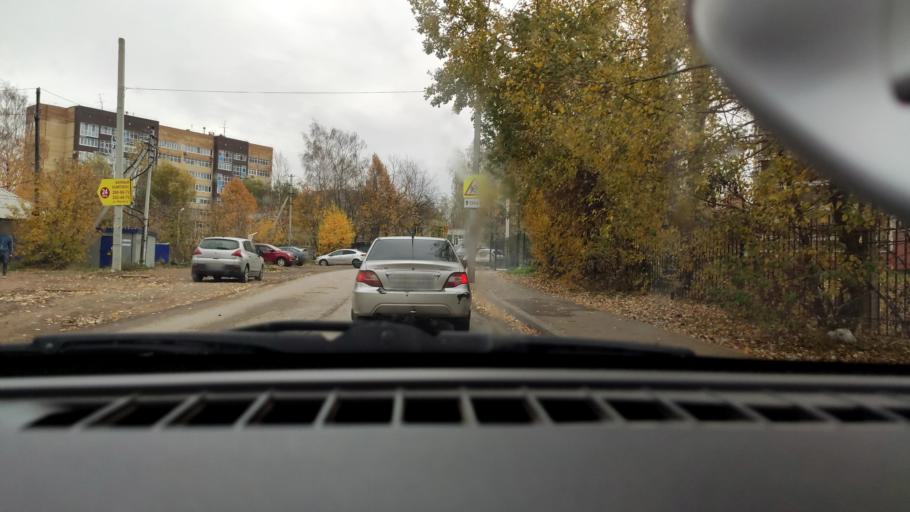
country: RU
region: Perm
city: Perm
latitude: 57.9881
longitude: 56.2236
